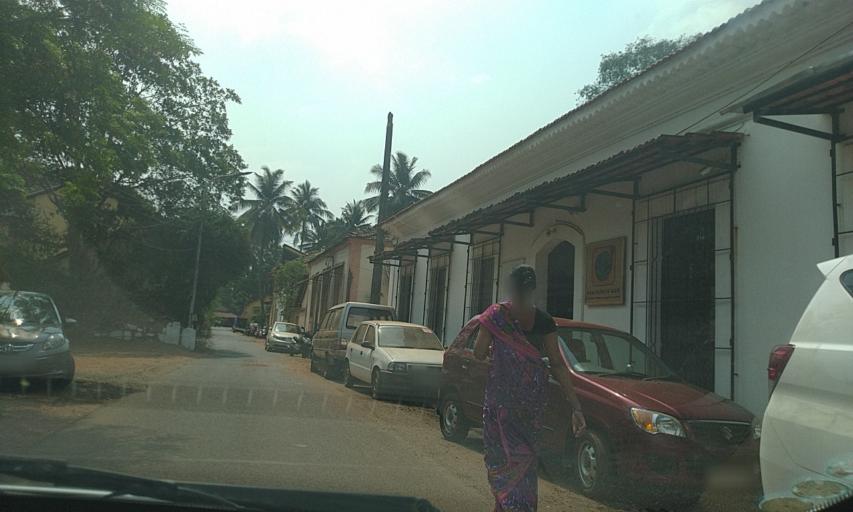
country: IN
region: Goa
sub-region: North Goa
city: Panaji
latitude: 15.4903
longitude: 73.8297
